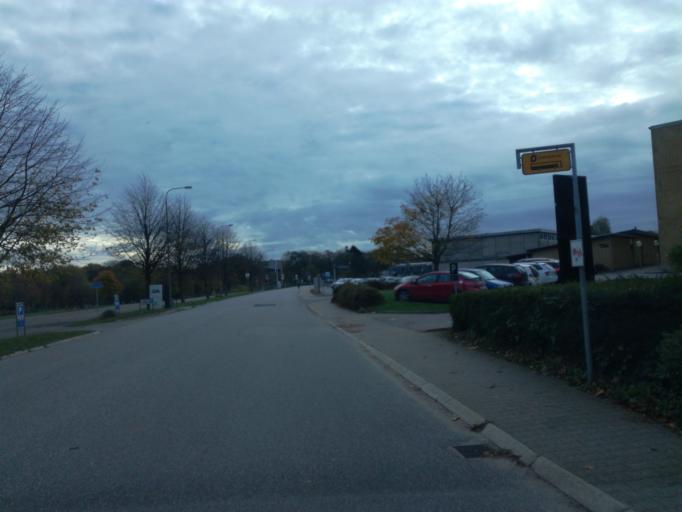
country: DK
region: South Denmark
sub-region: Fredericia Kommune
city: Fredericia
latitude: 55.5713
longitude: 9.7340
